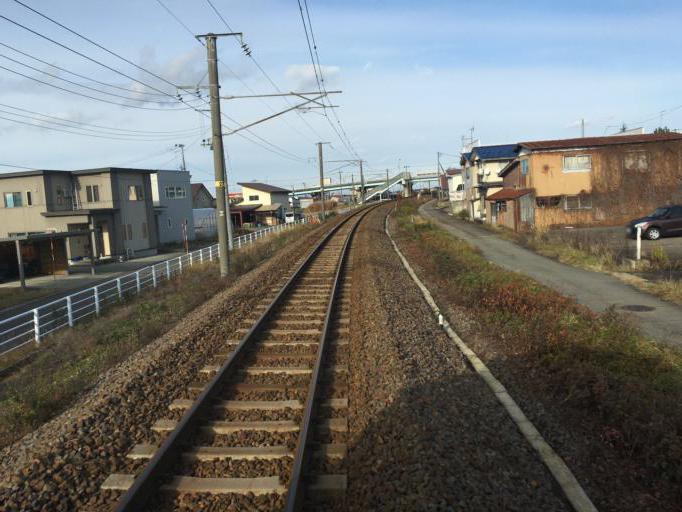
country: JP
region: Akita
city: Yuzawa
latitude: 39.1681
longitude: 140.4875
